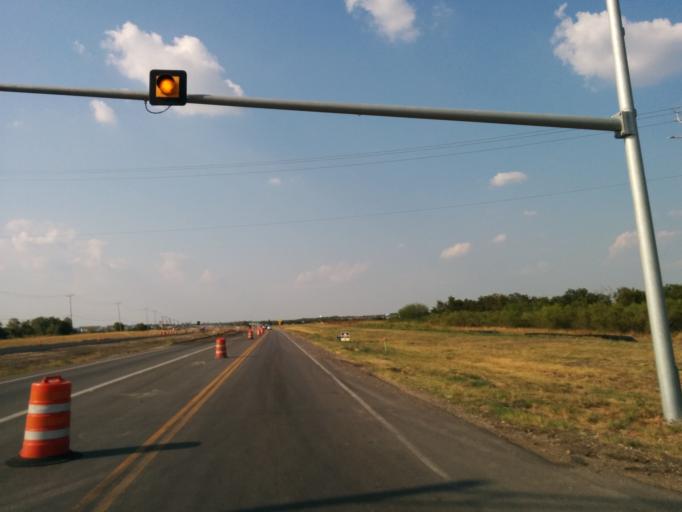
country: US
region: Texas
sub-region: Bexar County
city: Converse
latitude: 29.4913
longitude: -98.2903
